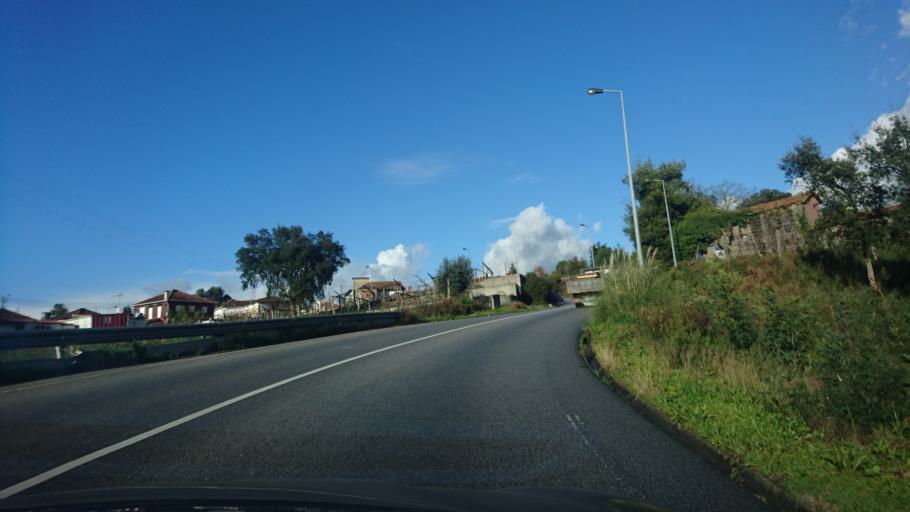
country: PT
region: Porto
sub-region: Paredes
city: Recarei
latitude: 41.1524
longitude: -8.4011
